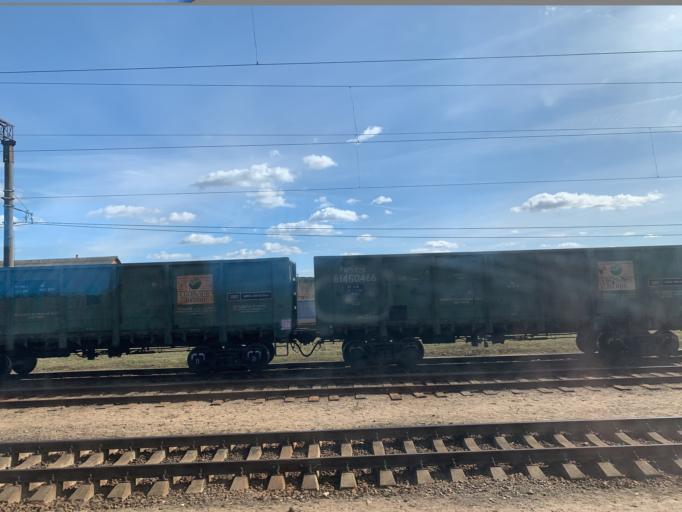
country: BY
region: Minsk
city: Stowbtsy
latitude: 53.4810
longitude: 26.7540
